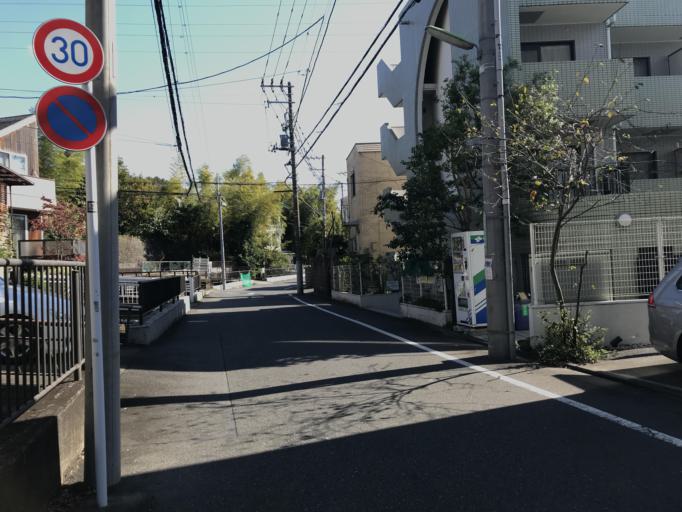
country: JP
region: Tokyo
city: Tokyo
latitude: 35.6042
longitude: 139.6394
